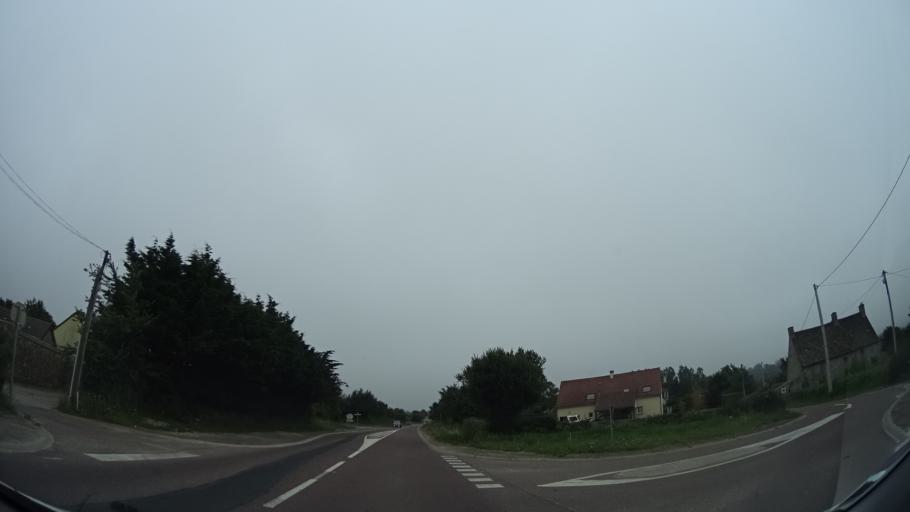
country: FR
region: Lower Normandy
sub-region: Departement de la Manche
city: Les Pieux
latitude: 49.5363
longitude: -1.8317
